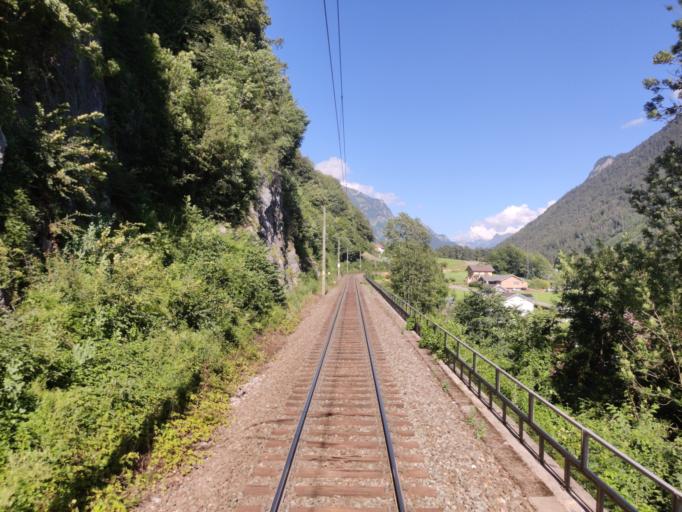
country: AT
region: Vorarlberg
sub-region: Politischer Bezirk Bludenz
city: Stallehr
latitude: 47.1450
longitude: 9.8618
